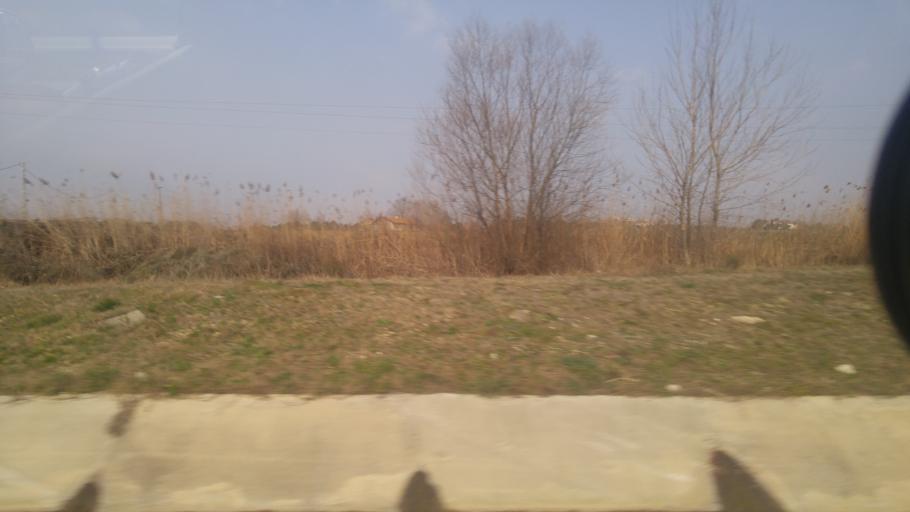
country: TR
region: Istanbul
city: Kumburgaz
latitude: 41.0094
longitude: 28.5032
